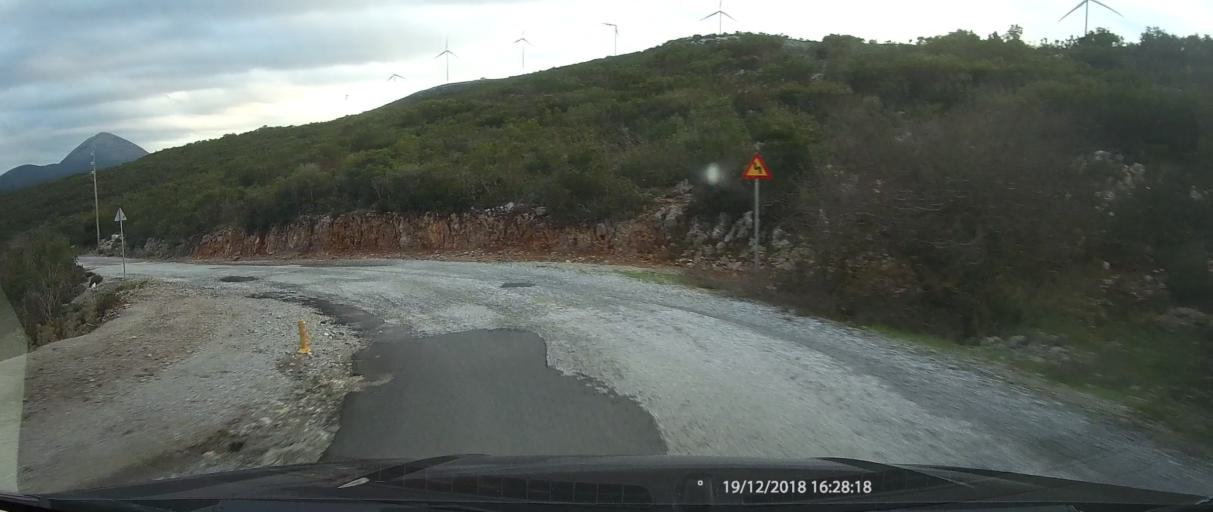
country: GR
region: Peloponnese
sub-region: Nomos Lakonias
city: Kato Glikovrisi
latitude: 36.9602
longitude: 22.8638
